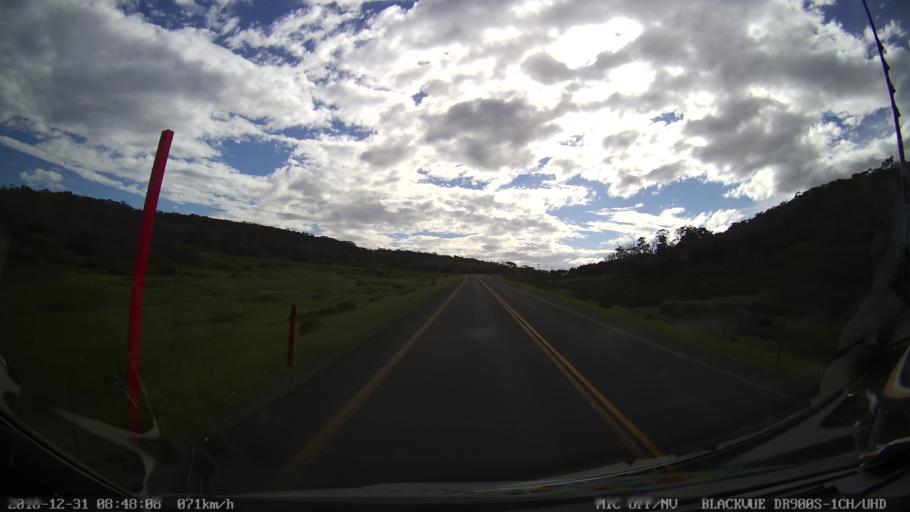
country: AU
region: New South Wales
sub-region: Snowy River
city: Jindabyne
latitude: -36.3591
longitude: 148.4926
